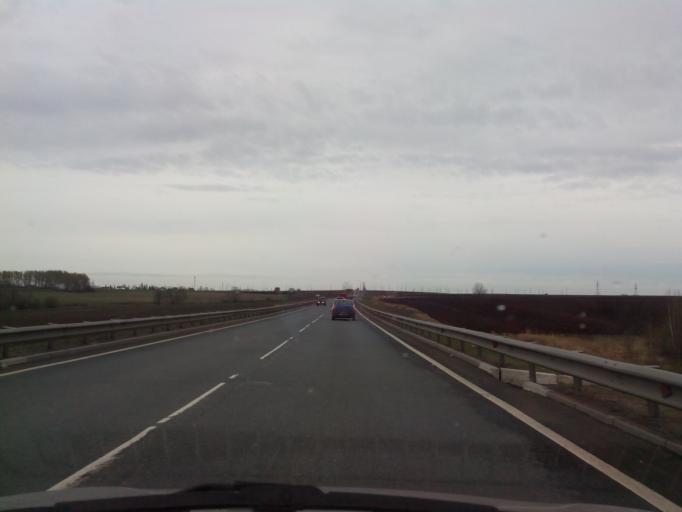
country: RU
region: Moskovskaya
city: Kashira
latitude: 54.7684
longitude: 38.1788
